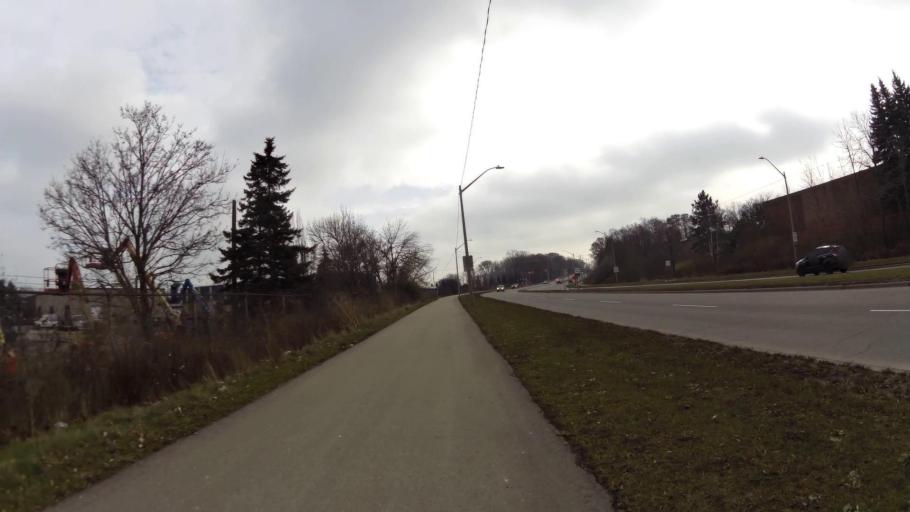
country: CA
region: Ontario
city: Kitchener
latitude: 43.4249
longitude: -80.4780
